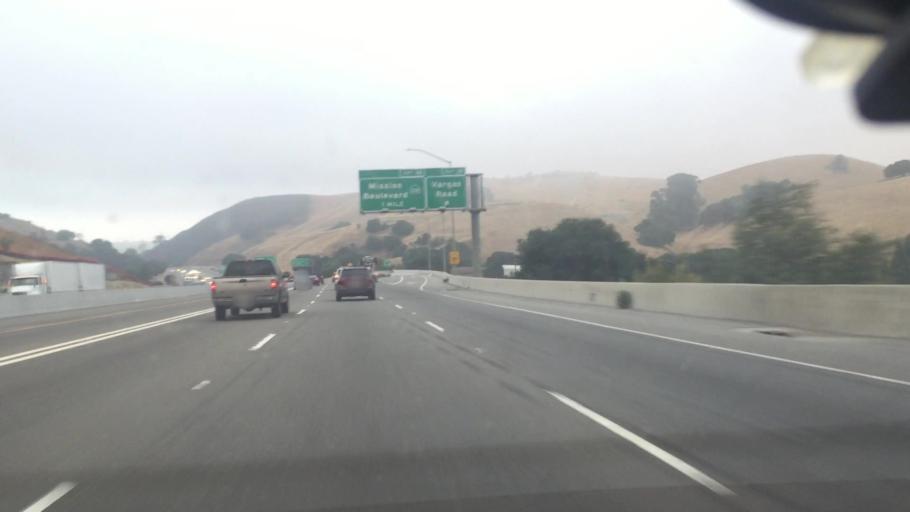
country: US
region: California
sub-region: Alameda County
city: Fremont
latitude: 37.5568
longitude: -121.9154
